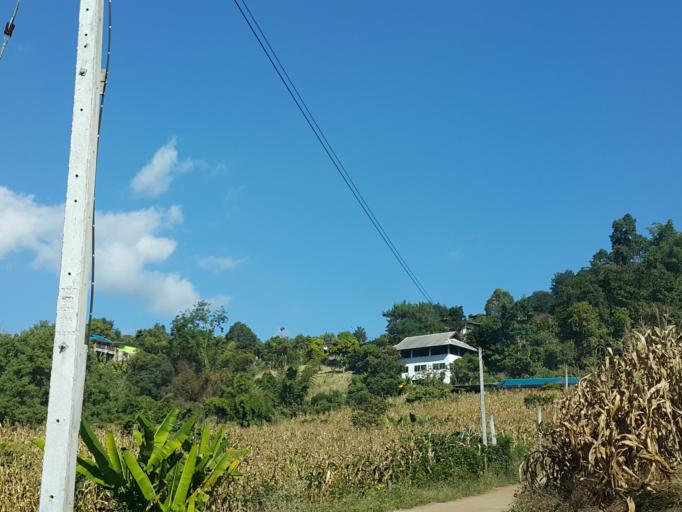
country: TH
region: Chiang Mai
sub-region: Amphoe Chiang Dao
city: Chiang Dao
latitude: 19.5221
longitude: 98.8627
